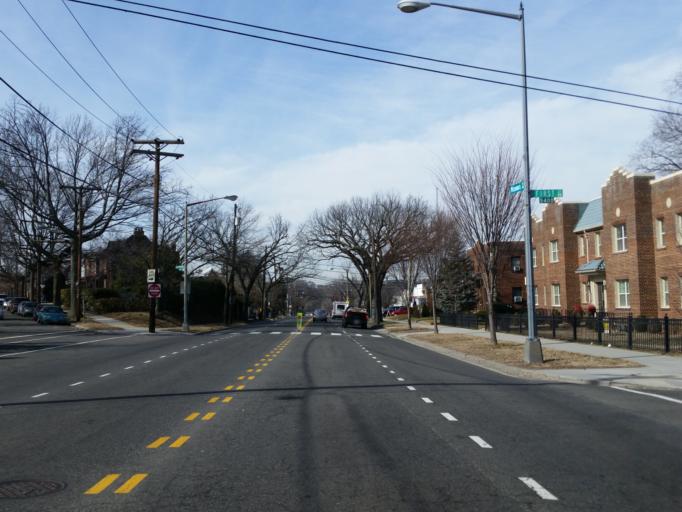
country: US
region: Maryland
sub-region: Prince George's County
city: Chillum
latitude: 38.9556
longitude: -77.0115
